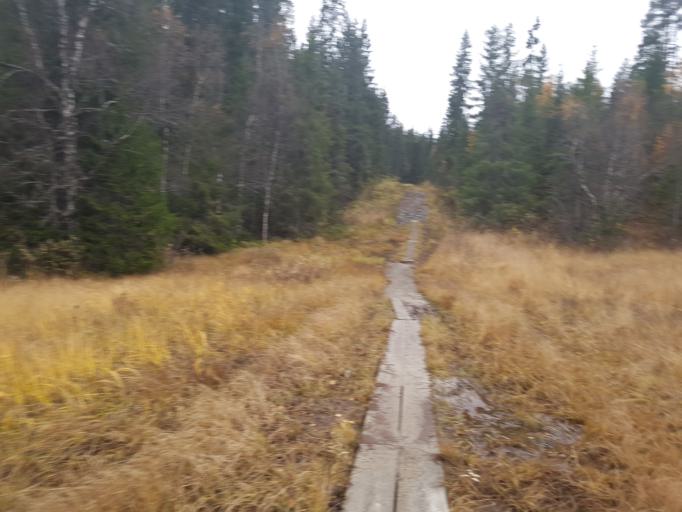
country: NO
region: Sor-Trondelag
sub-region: Melhus
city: Melhus
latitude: 63.3865
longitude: 10.2425
